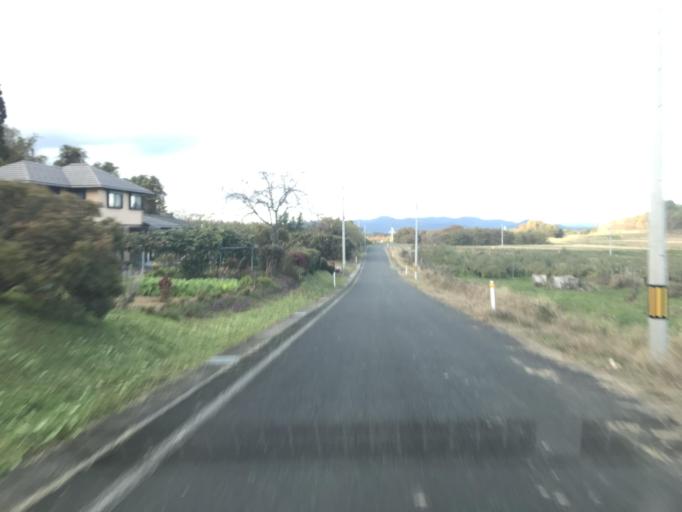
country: JP
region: Iwate
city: Ichinoseki
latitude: 38.8813
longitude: 141.1620
